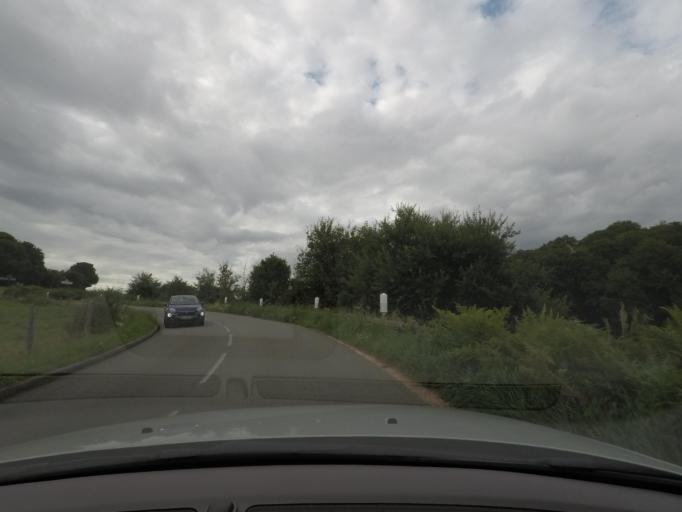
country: FR
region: Haute-Normandie
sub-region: Departement de l'Eure
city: Les Andelys
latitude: 49.2847
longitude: 1.3482
